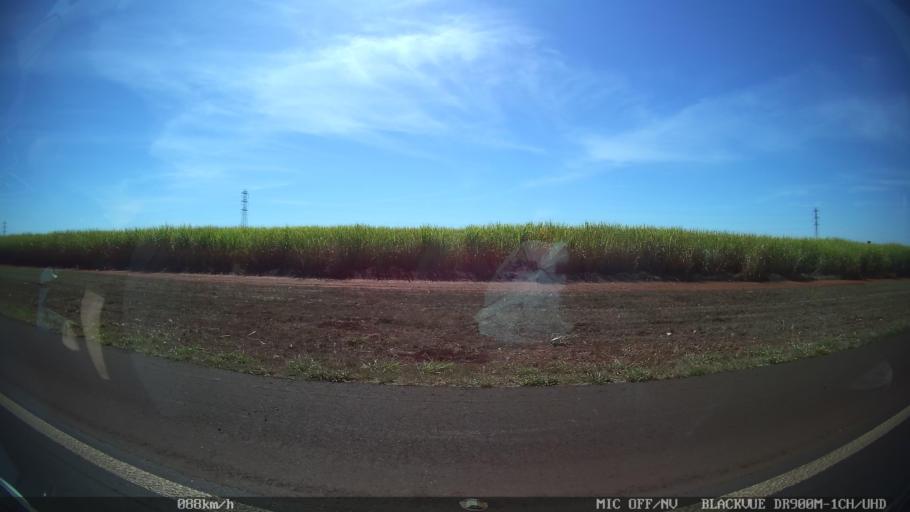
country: BR
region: Sao Paulo
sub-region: Guaira
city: Guaira
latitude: -20.4450
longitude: -48.2353
